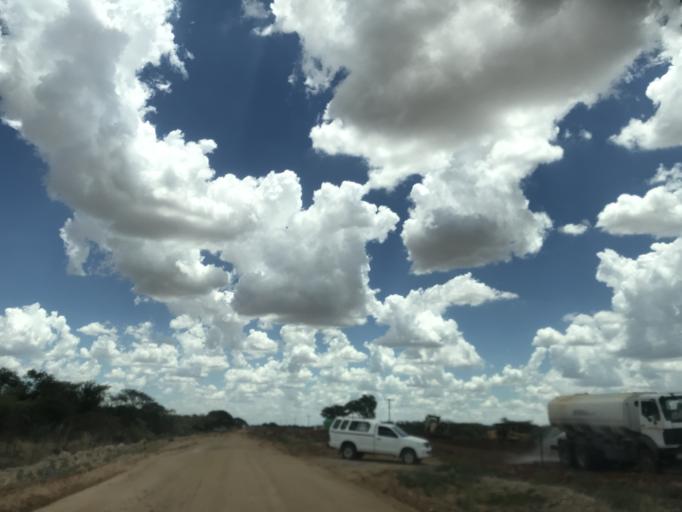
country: BW
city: Mabuli
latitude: -25.7898
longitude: 24.6453
